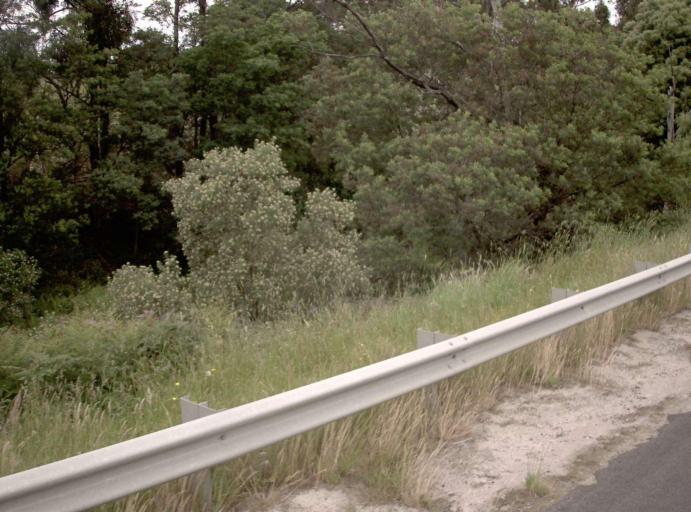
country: AU
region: Victoria
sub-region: Baw Baw
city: Warragul
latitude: -38.4558
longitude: 145.9285
